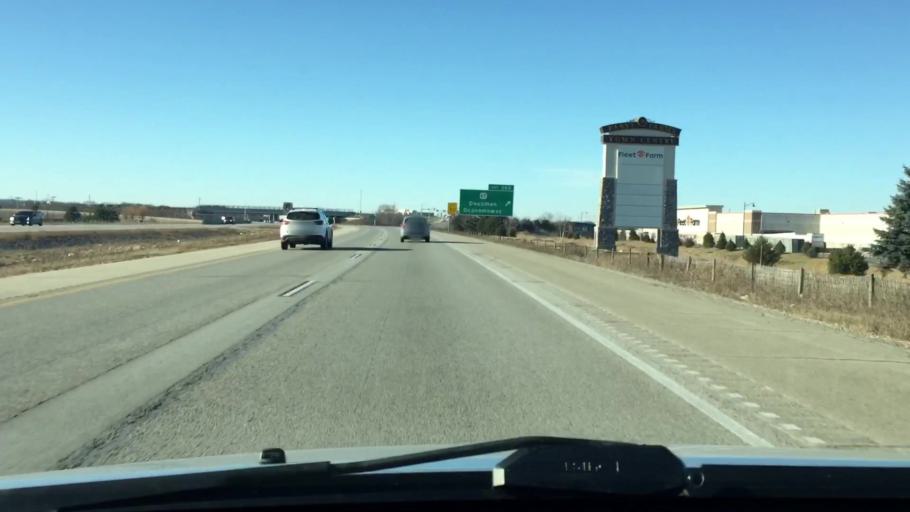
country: US
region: Wisconsin
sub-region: Waukesha County
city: Dousman
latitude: 43.0678
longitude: -88.4640
